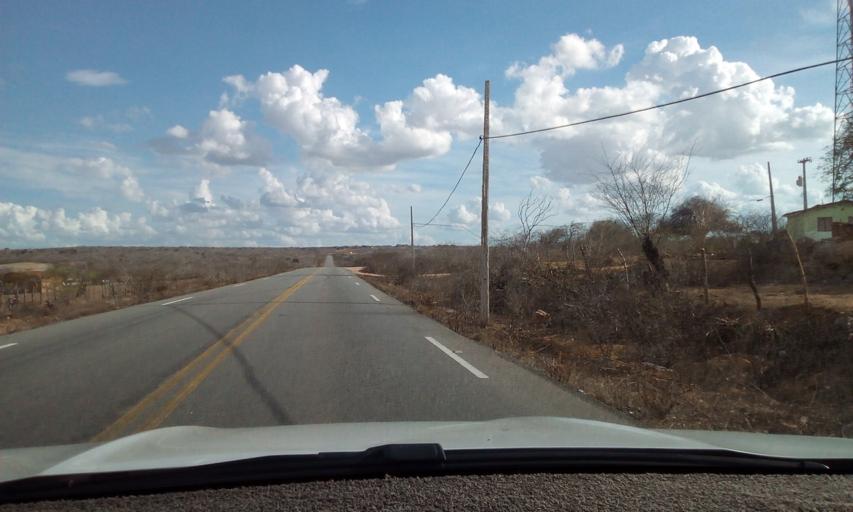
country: BR
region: Paraiba
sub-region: Soledade
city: Soledade
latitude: -6.8649
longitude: -36.4026
